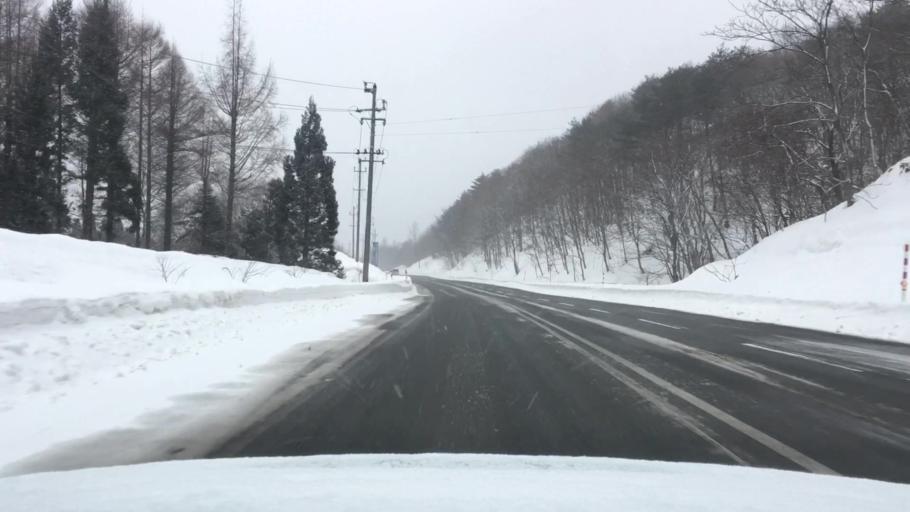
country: JP
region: Akita
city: Hanawa
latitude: 40.0189
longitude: 140.9893
